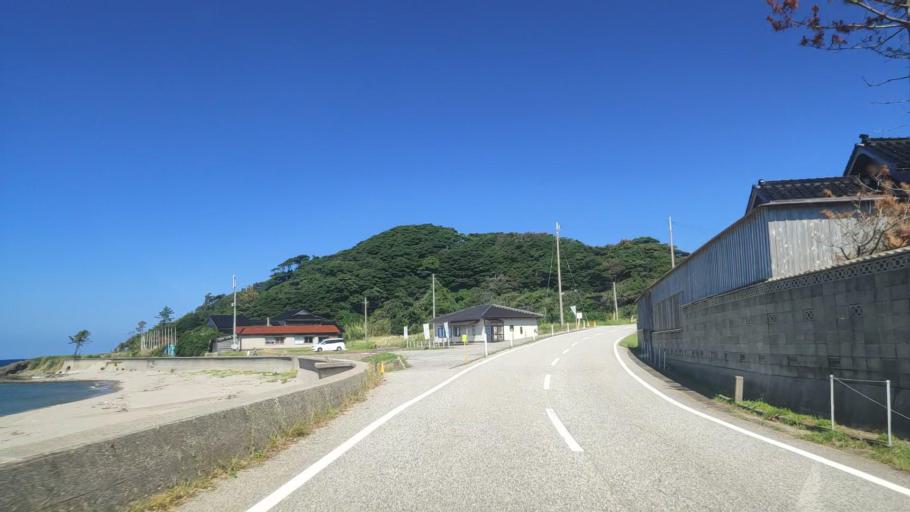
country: JP
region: Ishikawa
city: Nanao
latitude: 37.5119
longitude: 137.2197
